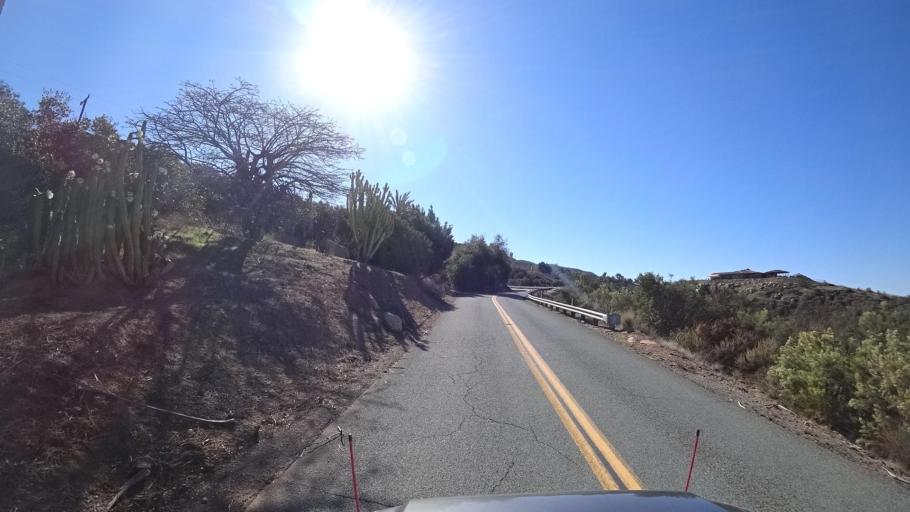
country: US
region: California
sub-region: San Diego County
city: Jamul
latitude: 32.7291
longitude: -116.8365
